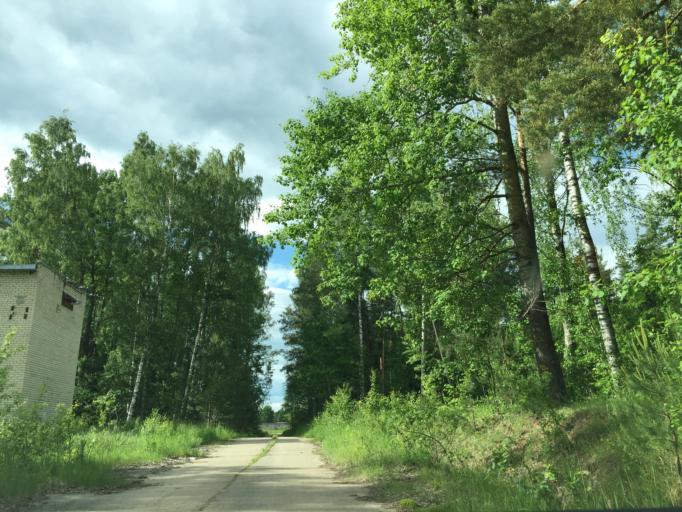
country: LV
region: Dobeles Rajons
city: Dobele
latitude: 56.6388
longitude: 23.1752
